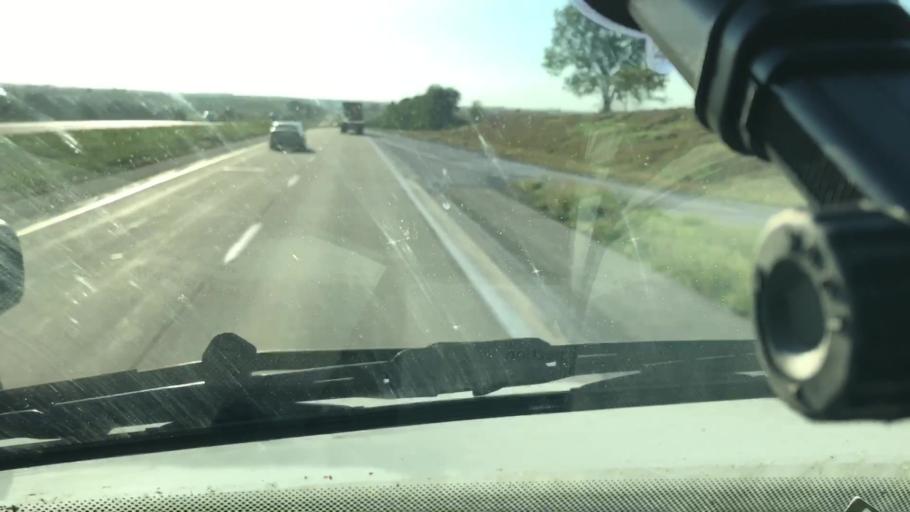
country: US
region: Iowa
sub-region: Pottawattamie County
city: Avoca
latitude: 41.4978
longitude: -95.5502
